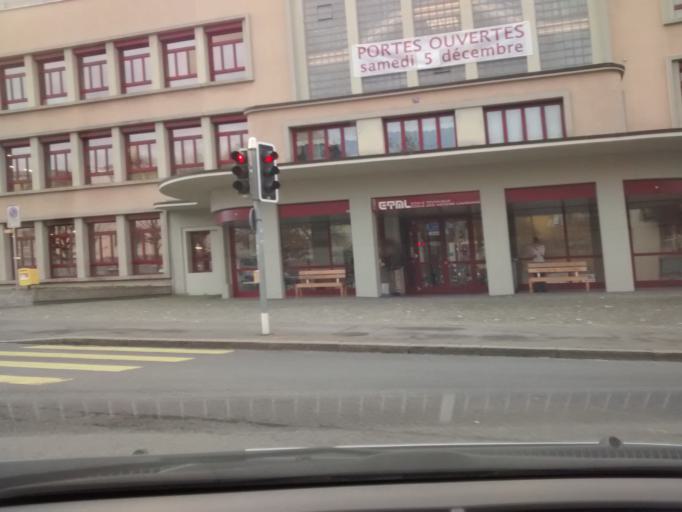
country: CH
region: Vaud
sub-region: Lausanne District
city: Blecherette
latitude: 46.5244
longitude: 6.6161
